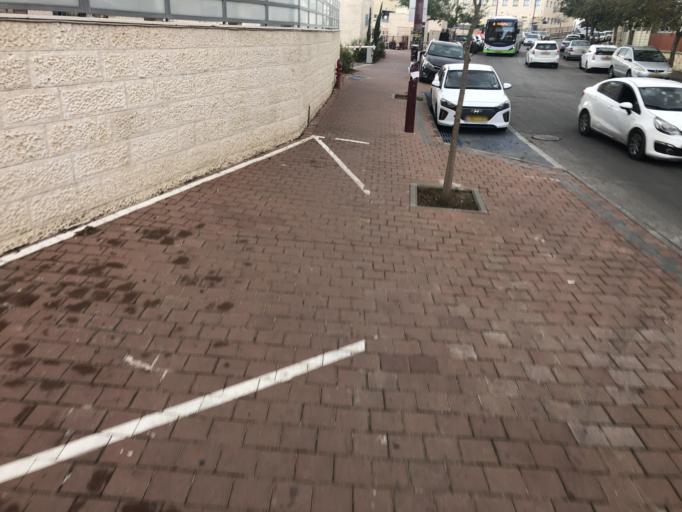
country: IL
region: Jerusalem
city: Modiin Ilit
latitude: 31.9374
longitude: 35.0407
